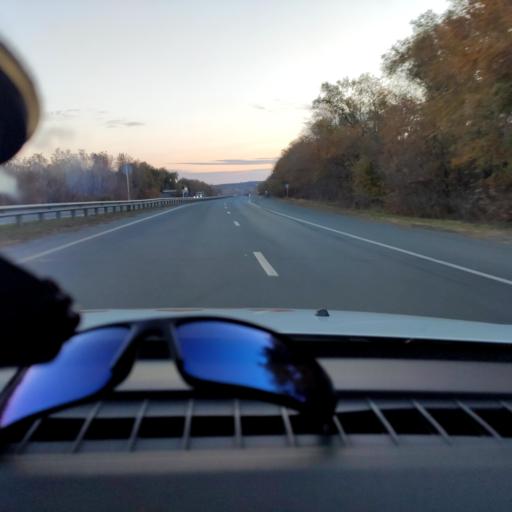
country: RU
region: Samara
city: Novokuybyshevsk
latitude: 53.0515
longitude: 50.0109
